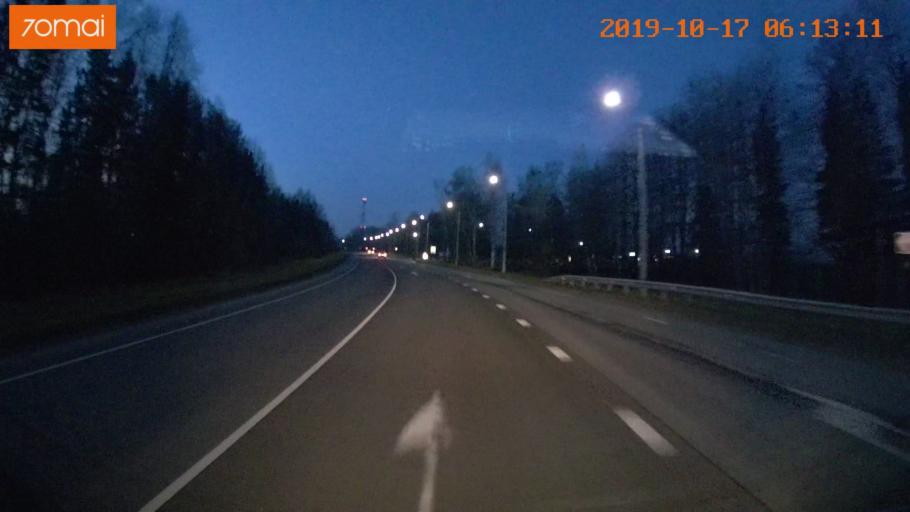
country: RU
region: Ivanovo
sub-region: Gorod Ivanovo
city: Ivanovo
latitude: 56.9018
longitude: 40.9376
